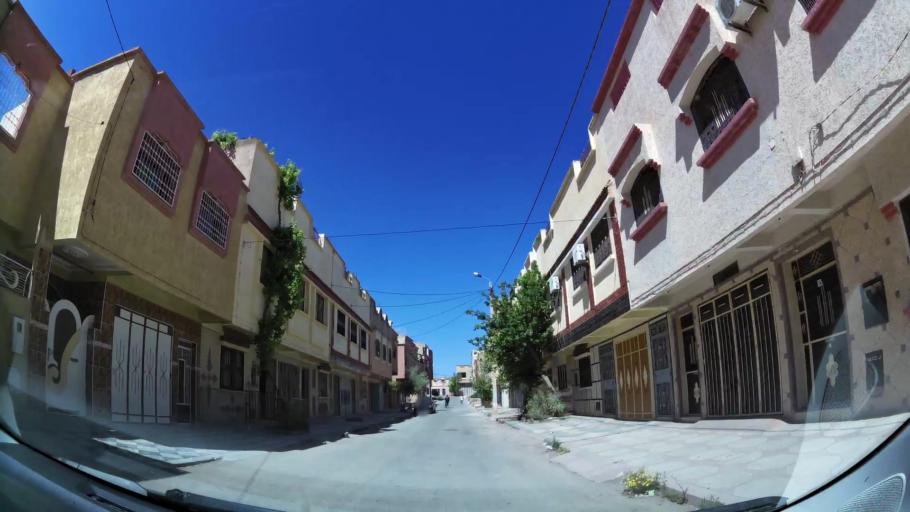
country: MA
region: Oriental
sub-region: Oujda-Angad
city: Oujda
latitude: 34.6646
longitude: -1.8891
